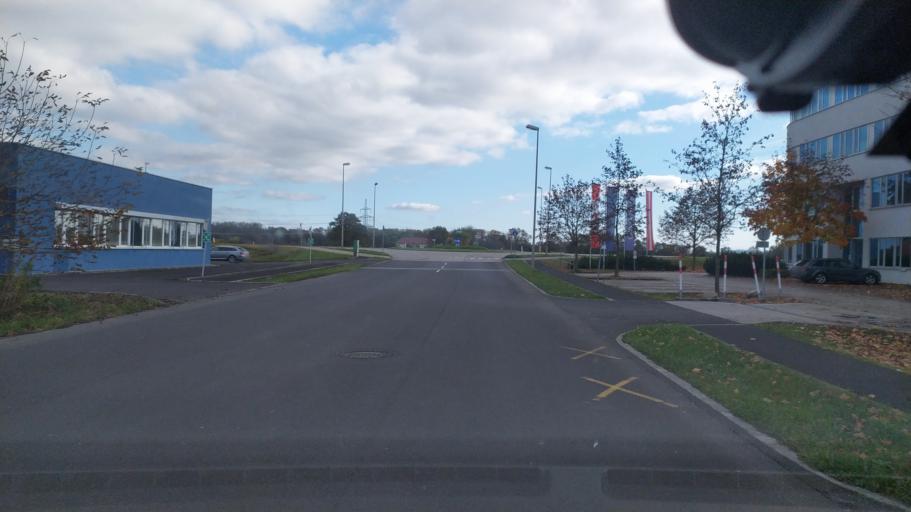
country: AT
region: Upper Austria
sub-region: Politischer Bezirk Urfahr-Umgebung
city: Steyregg
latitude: 48.2493
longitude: 14.3817
